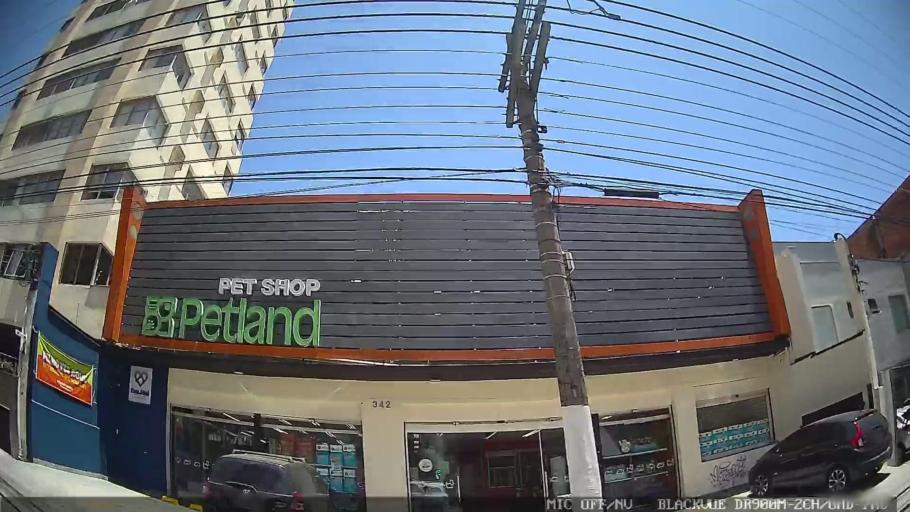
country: BR
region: Sao Paulo
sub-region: Sao Paulo
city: Sao Paulo
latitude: -23.5583
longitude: -46.6004
